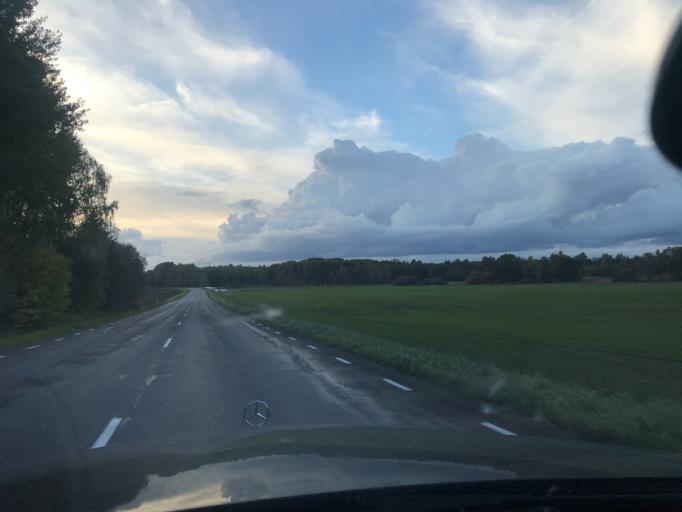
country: EE
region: Vorumaa
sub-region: Antsla vald
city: Vana-Antsla
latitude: 57.9030
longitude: 26.4667
